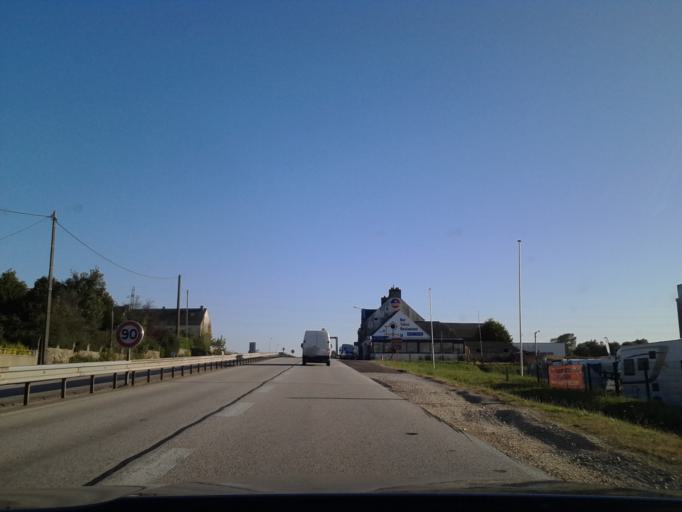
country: FR
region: Lower Normandy
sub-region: Departement de la Manche
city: La Glacerie
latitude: 49.5948
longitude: -1.5958
